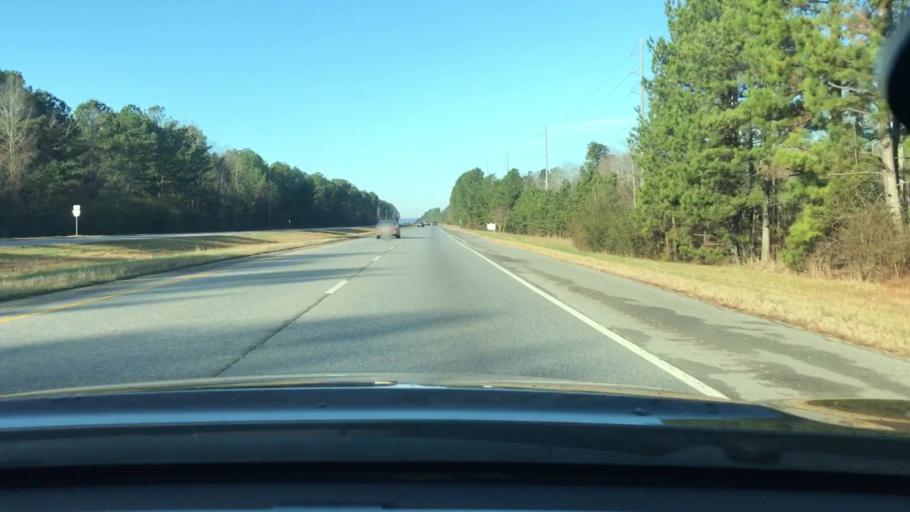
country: US
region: Alabama
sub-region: Shelby County
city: Westover
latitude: 33.3488
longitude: -86.5728
